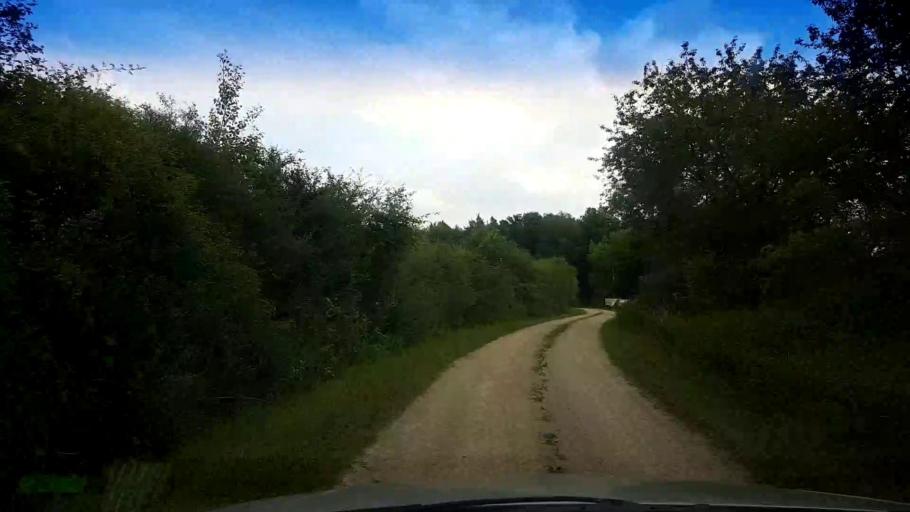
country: DE
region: Bavaria
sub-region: Upper Franconia
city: Stegaurach
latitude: 49.8775
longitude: 10.8150
